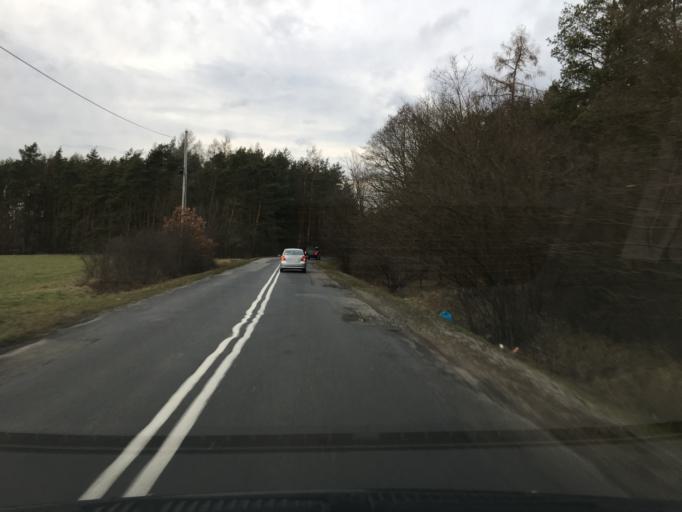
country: PL
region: Opole Voivodeship
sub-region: Powiat kedzierzynsko-kozielski
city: Kozle
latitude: 50.3650
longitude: 18.1576
